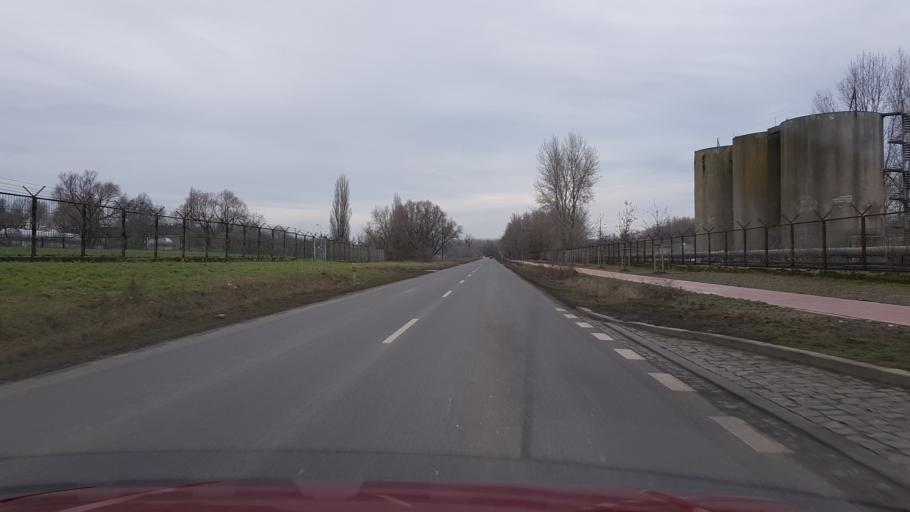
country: PL
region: West Pomeranian Voivodeship
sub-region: Powiat policki
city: Police
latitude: 53.5787
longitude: 14.5540
